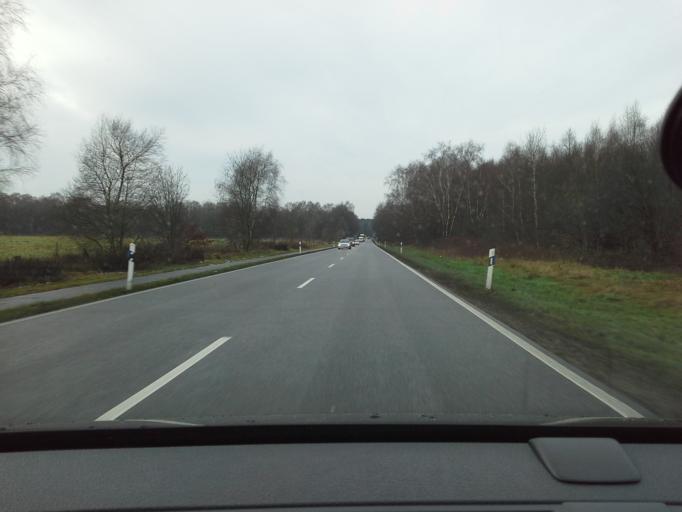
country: DE
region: Schleswig-Holstein
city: Henstedt-Ulzburg
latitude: 53.7438
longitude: 10.0177
